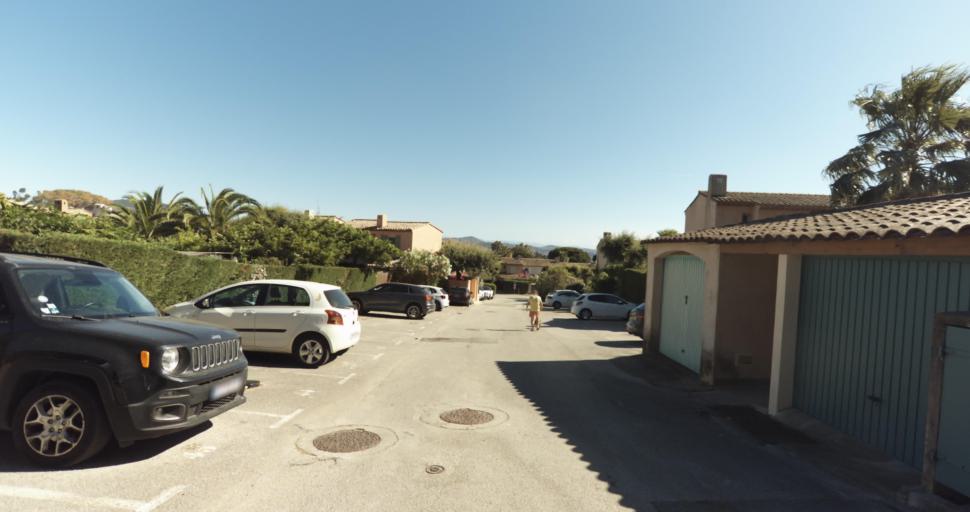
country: FR
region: Provence-Alpes-Cote d'Azur
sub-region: Departement du Var
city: Saint-Tropez
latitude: 43.2602
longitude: 6.6178
